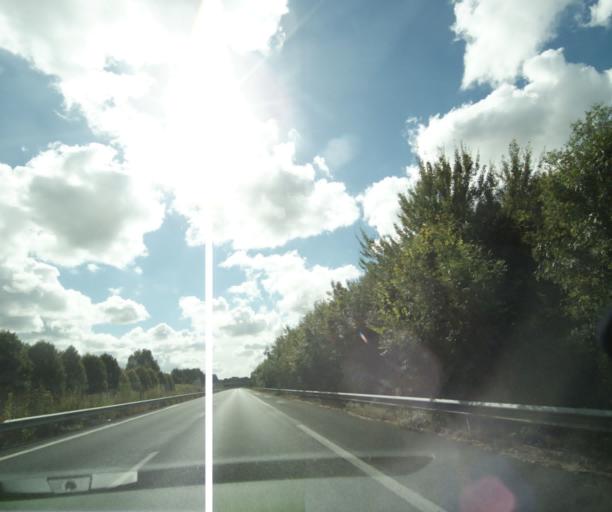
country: FR
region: Poitou-Charentes
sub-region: Departement de la Charente-Maritime
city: Cabariot
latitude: 45.9405
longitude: -0.8459
